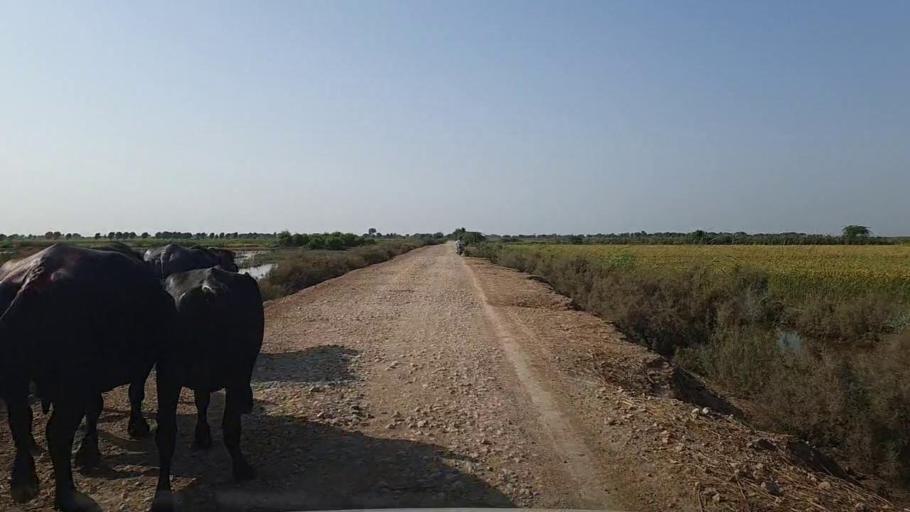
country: PK
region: Sindh
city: Kario
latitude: 24.8085
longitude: 68.5082
